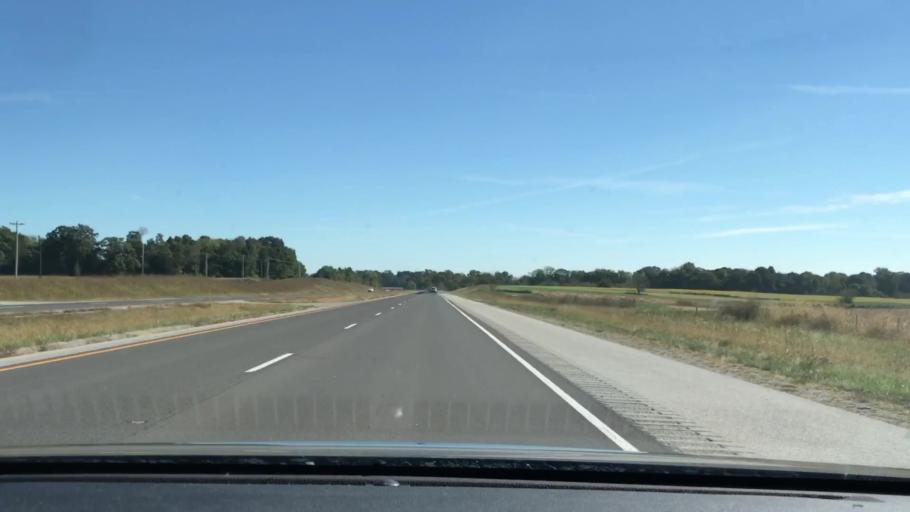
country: US
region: Kentucky
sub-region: Todd County
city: Elkton
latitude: 36.8137
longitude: -87.0198
